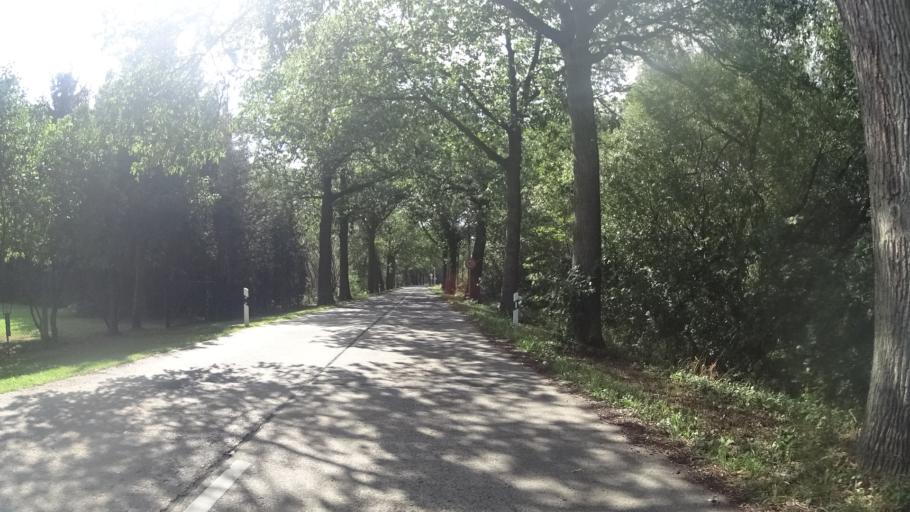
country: DE
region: Brandenburg
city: Ruhstadt
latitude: 52.9160
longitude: 11.8692
